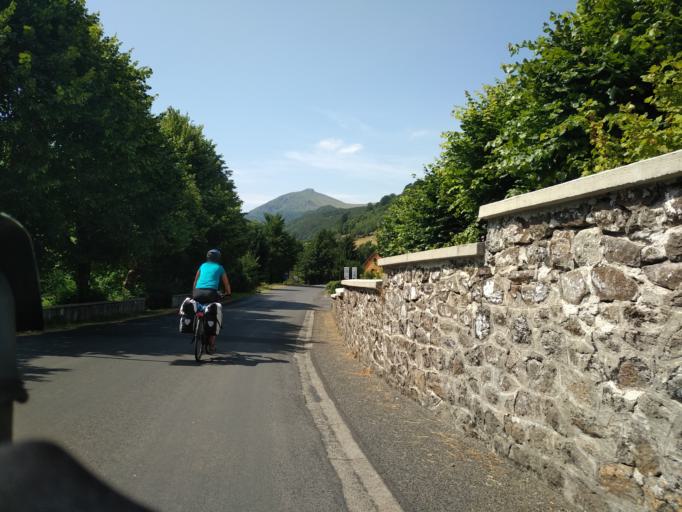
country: FR
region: Auvergne
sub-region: Departement du Cantal
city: Riom-es-Montagnes
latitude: 45.1582
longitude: 2.7054
